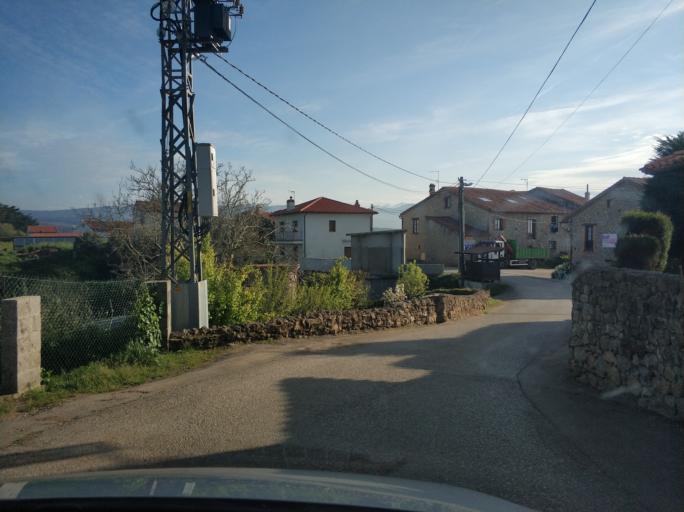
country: ES
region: Cantabria
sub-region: Provincia de Cantabria
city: Comillas
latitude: 43.3842
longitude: -4.3132
